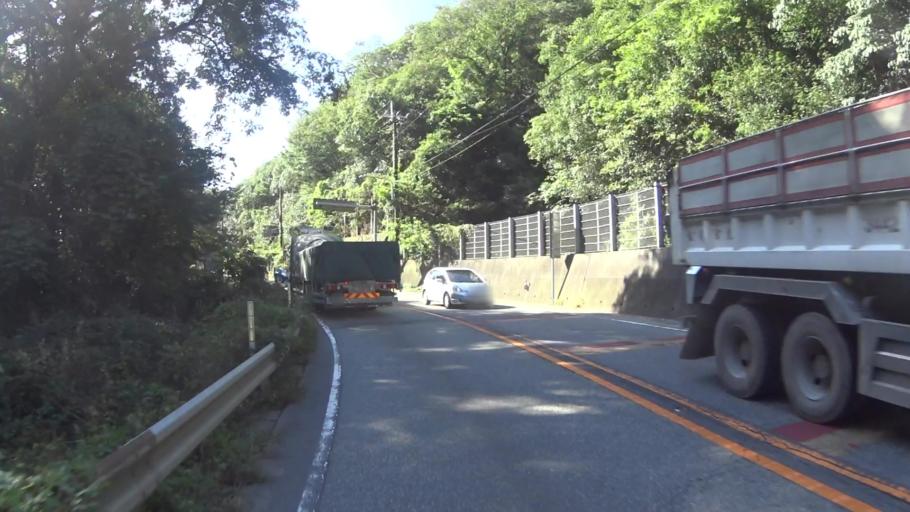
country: JP
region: Kyoto
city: Kameoka
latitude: 34.9860
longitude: 135.6380
